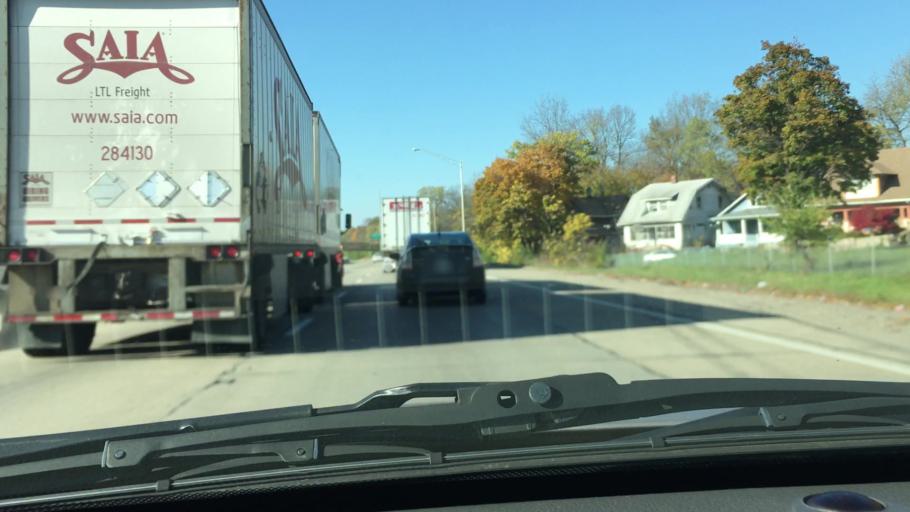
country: US
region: Indiana
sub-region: Marion County
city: Indianapolis
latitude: 39.8135
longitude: -86.1817
